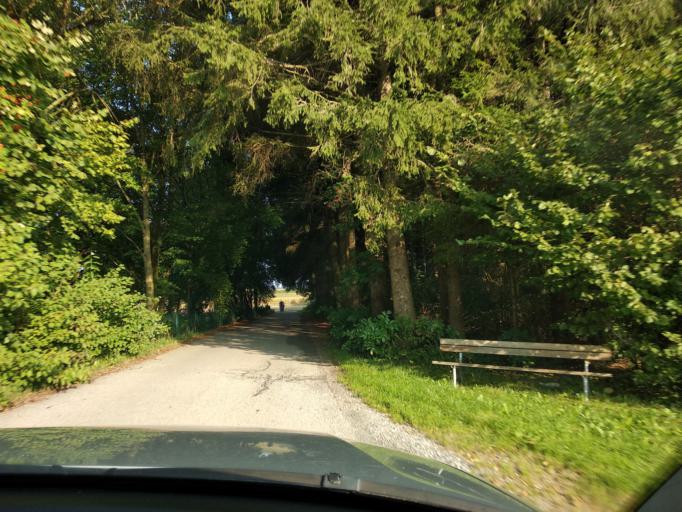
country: DE
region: Bavaria
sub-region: Upper Bavaria
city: Obing
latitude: 47.9968
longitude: 12.4188
